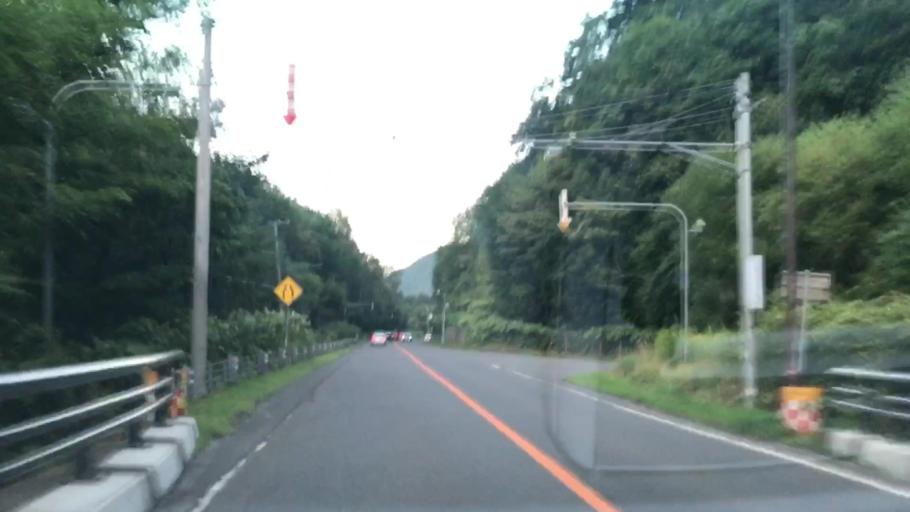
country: JP
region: Hokkaido
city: Sapporo
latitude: 42.9445
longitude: 141.1331
